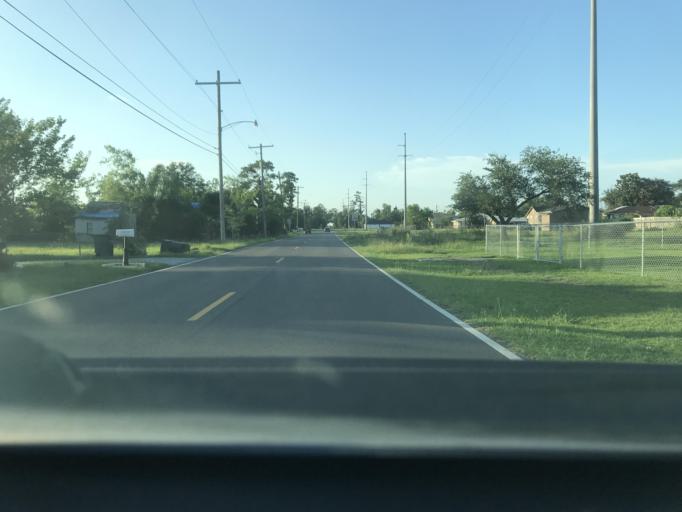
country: US
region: Louisiana
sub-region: Calcasieu Parish
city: Moss Bluff
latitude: 30.2576
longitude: -93.1954
